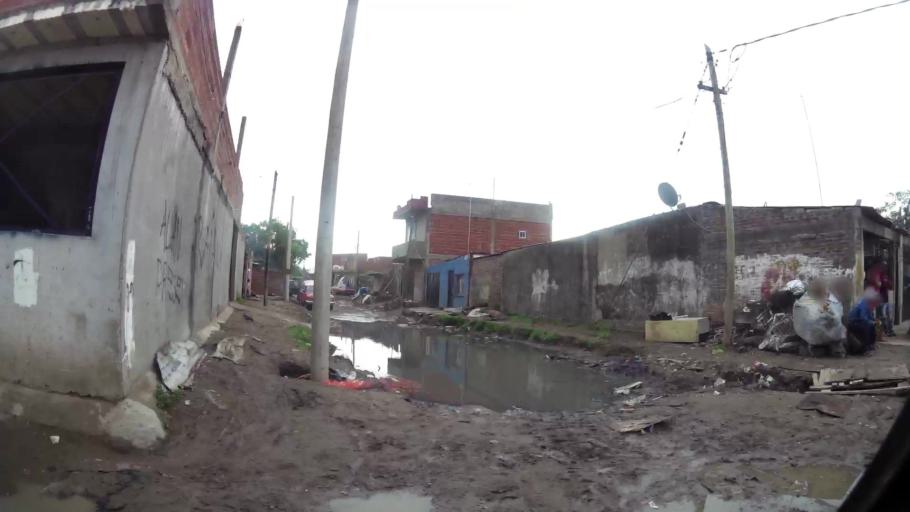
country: AR
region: Buenos Aires
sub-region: Partido de Lanus
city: Lanus
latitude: -34.7232
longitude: -58.3503
